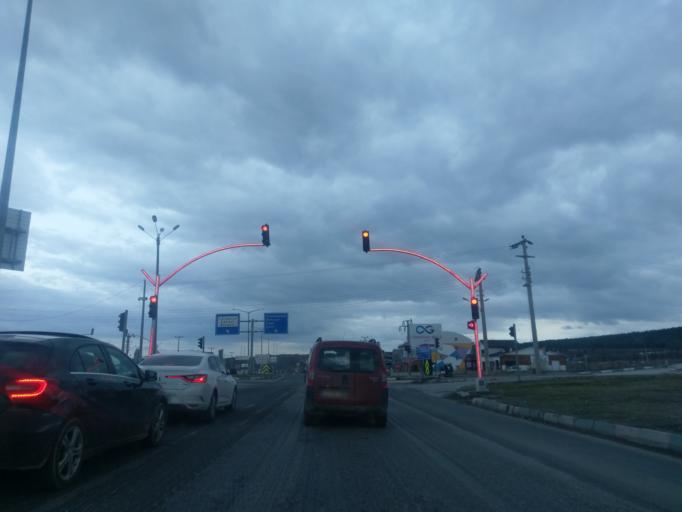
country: TR
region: Kuetahya
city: Kutahya
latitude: 39.3841
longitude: 30.0432
